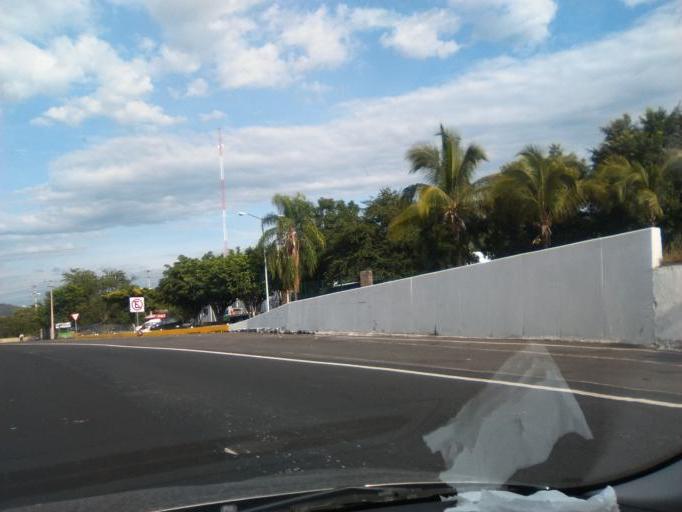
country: MX
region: Morelos
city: Alpuyeca
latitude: 18.7233
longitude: -99.2605
